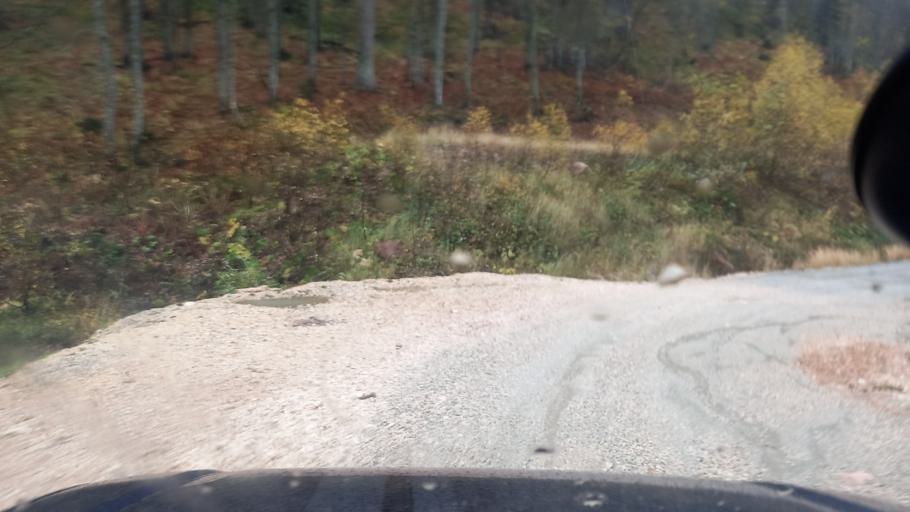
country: RU
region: Krasnodarskiy
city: Dagomys
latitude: 43.9835
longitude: 39.8516
